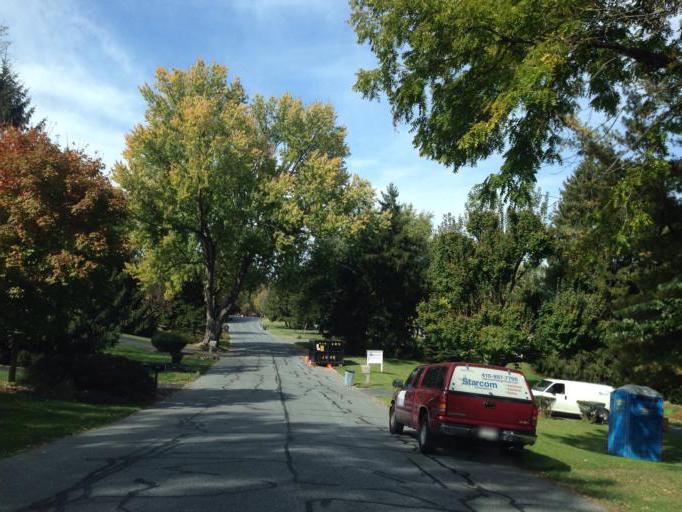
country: US
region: Maryland
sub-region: Howard County
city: Columbia
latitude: 39.2809
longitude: -76.8440
